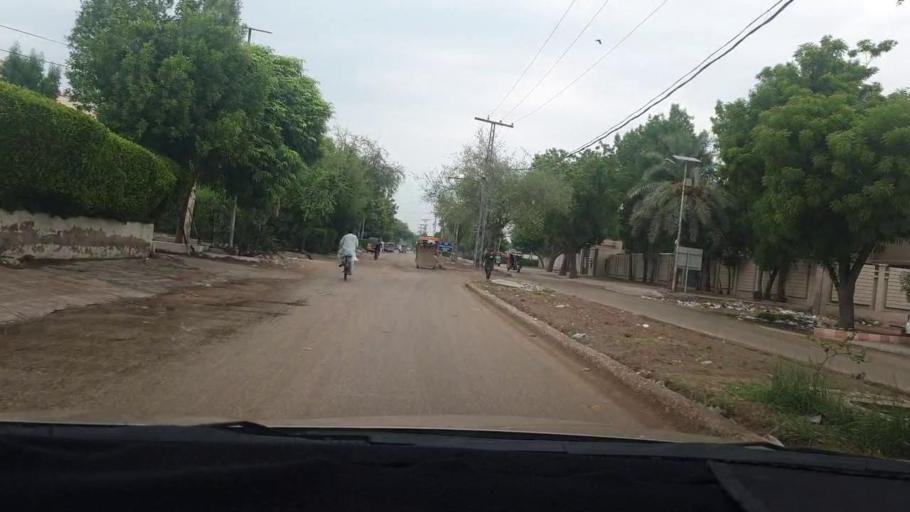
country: PK
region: Sindh
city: Larkana
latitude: 27.5605
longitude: 68.1973
